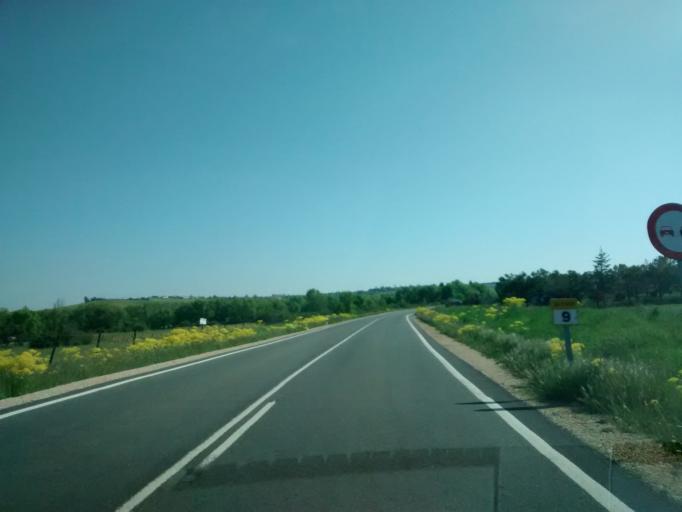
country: ES
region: Castille and Leon
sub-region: Provincia de Segovia
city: Trescasas
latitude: 40.9721
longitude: -4.0312
